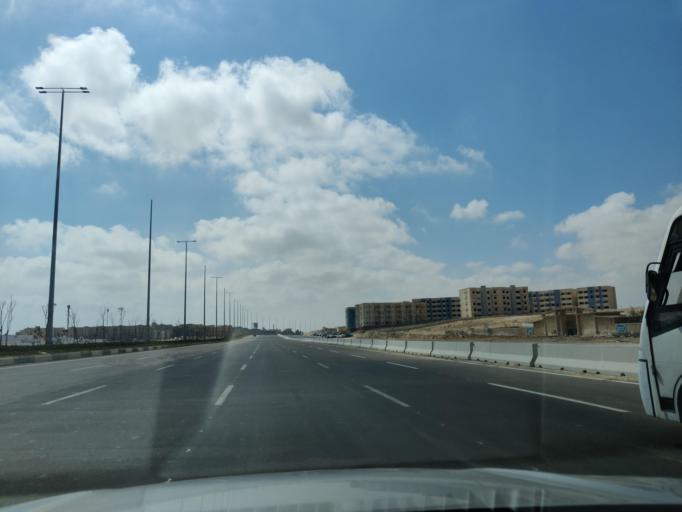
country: EG
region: Muhafazat Matruh
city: Al `Alamayn
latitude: 30.9590
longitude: 28.7610
